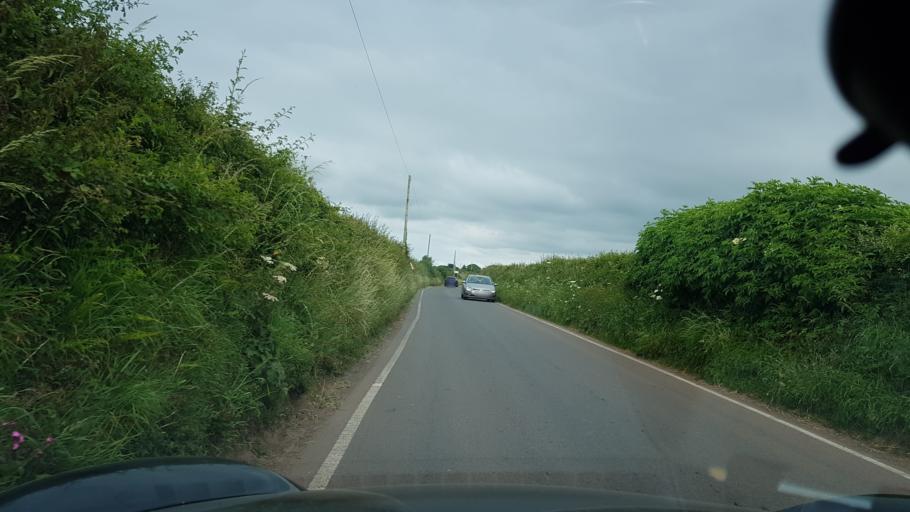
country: GB
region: Wales
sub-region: Pembrokeshire
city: Herbrandston
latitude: 51.7513
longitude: -5.1296
